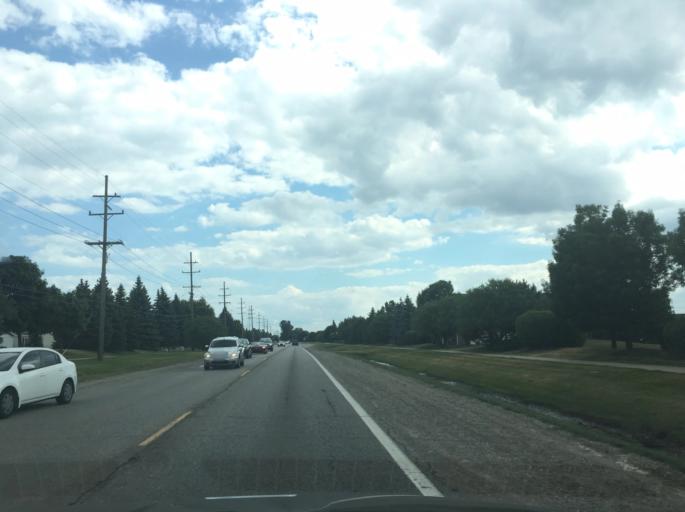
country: US
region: Michigan
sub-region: Macomb County
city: Clinton
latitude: 42.6374
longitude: -82.9561
